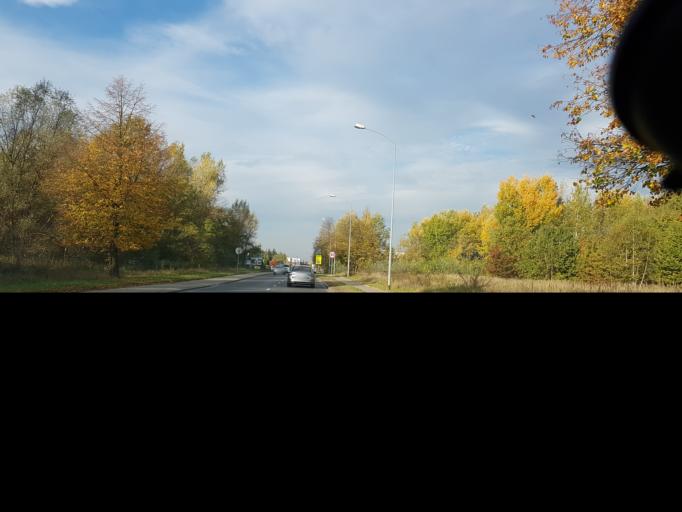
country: PL
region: Masovian Voivodeship
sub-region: Warszawa
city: Bielany
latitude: 52.2837
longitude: 20.9077
